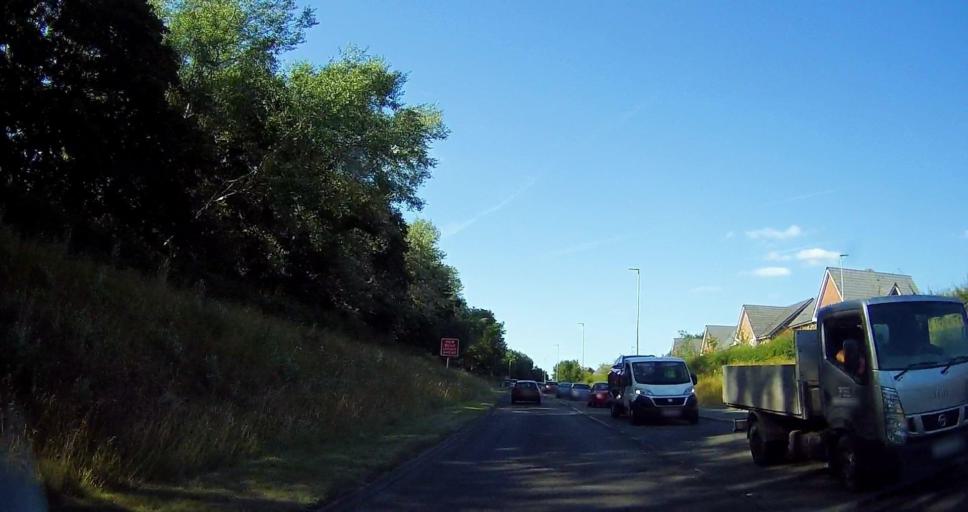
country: GB
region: England
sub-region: Cheshire East
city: Sandbach
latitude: 53.1481
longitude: -2.3520
